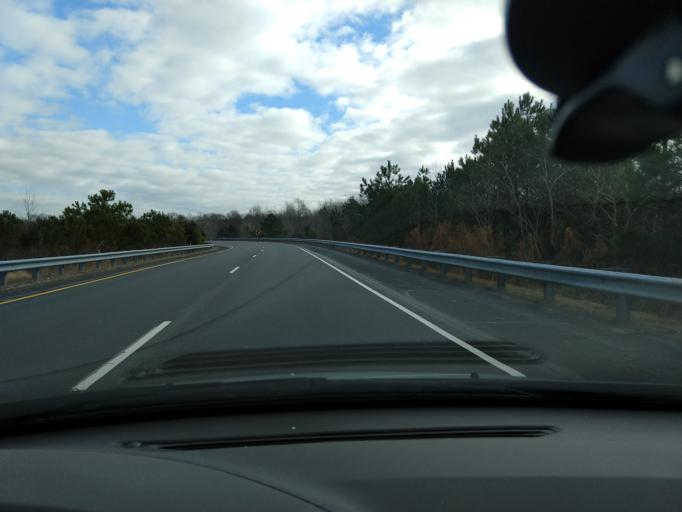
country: US
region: Virginia
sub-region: Chesterfield County
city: Bensley
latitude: 37.4560
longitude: -77.3861
